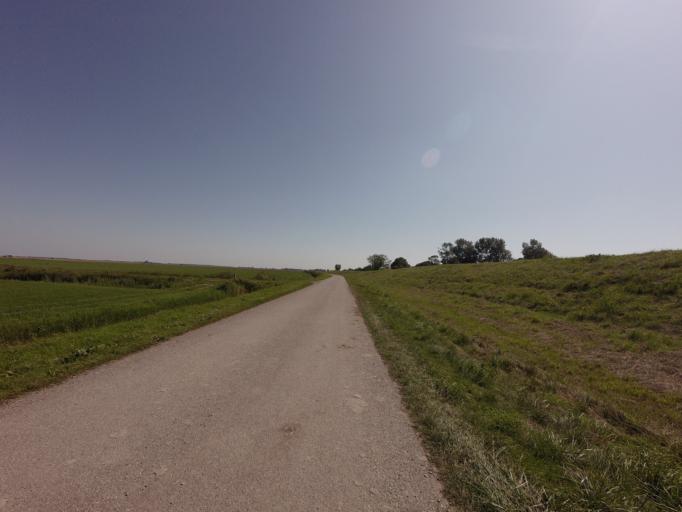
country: NL
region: Friesland
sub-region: Gemeente Dongeradeel
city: Anjum
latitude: 53.3934
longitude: 6.1141
